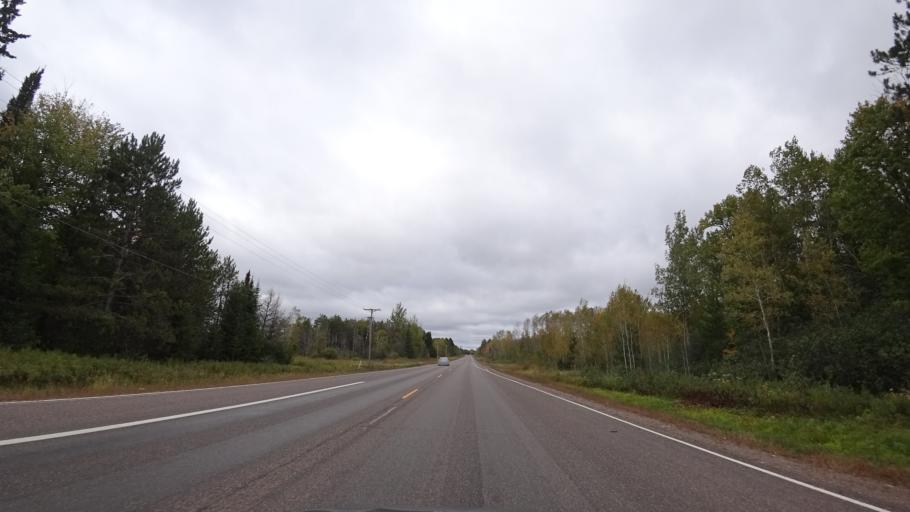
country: US
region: Wisconsin
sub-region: Rusk County
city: Ladysmith
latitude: 45.4368
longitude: -91.1109
